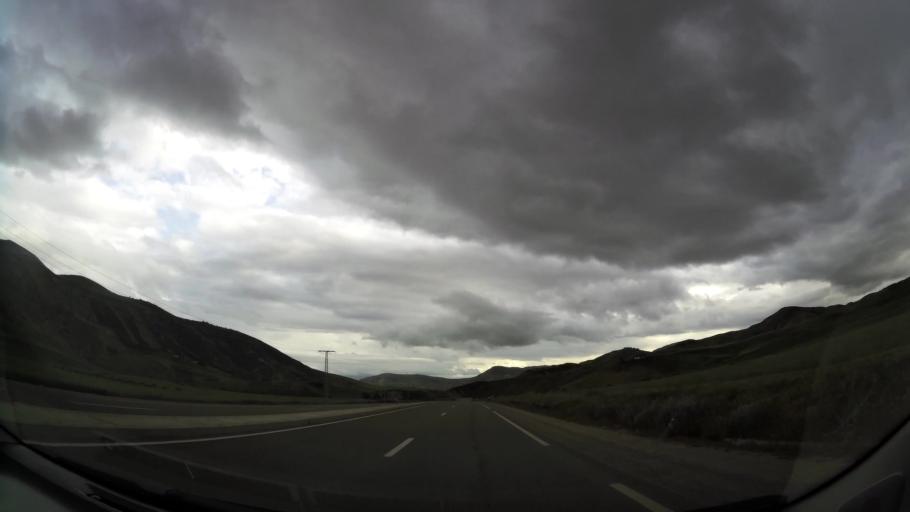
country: MA
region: Taza-Al Hoceima-Taounate
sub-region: Taza
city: Taza
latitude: 34.3308
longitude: -3.9472
